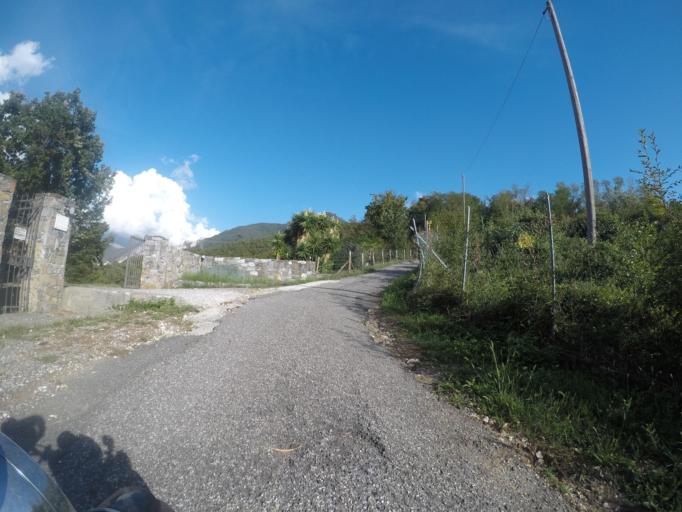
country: IT
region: Tuscany
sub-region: Provincia di Massa-Carrara
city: Massa
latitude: 44.0748
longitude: 10.1139
